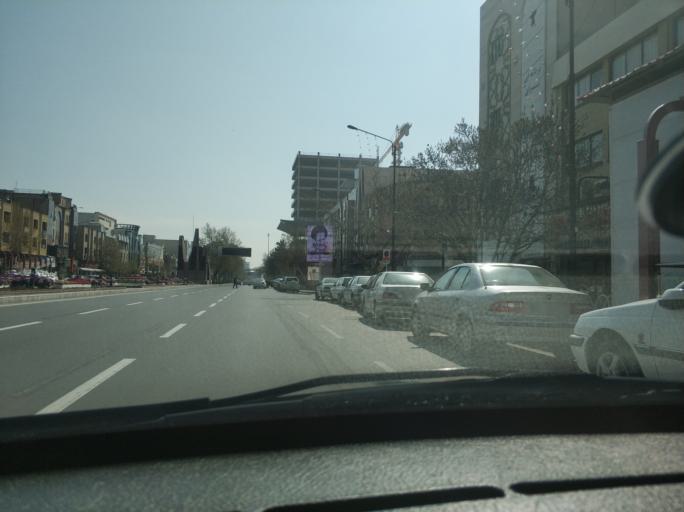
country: IR
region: Razavi Khorasan
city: Mashhad
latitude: 36.2944
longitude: 59.5783
